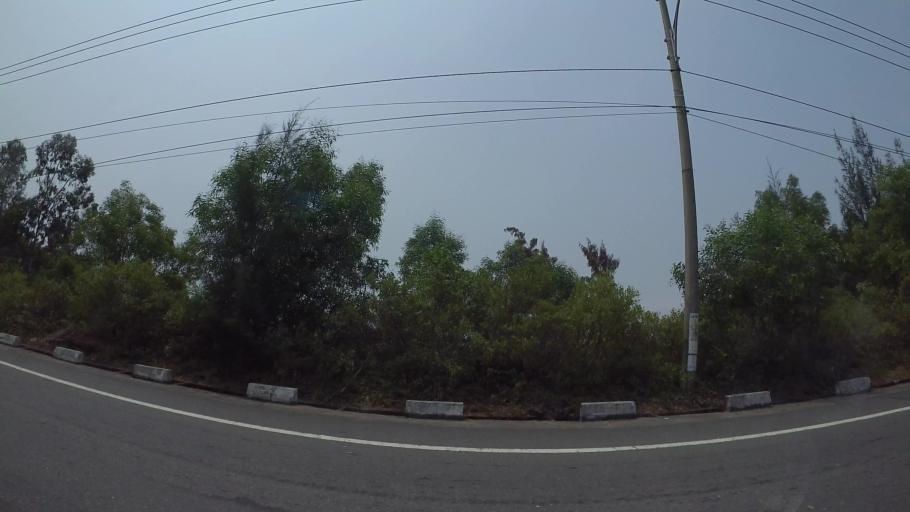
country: VN
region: Da Nang
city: Son Tra
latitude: 16.1000
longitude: 108.2695
